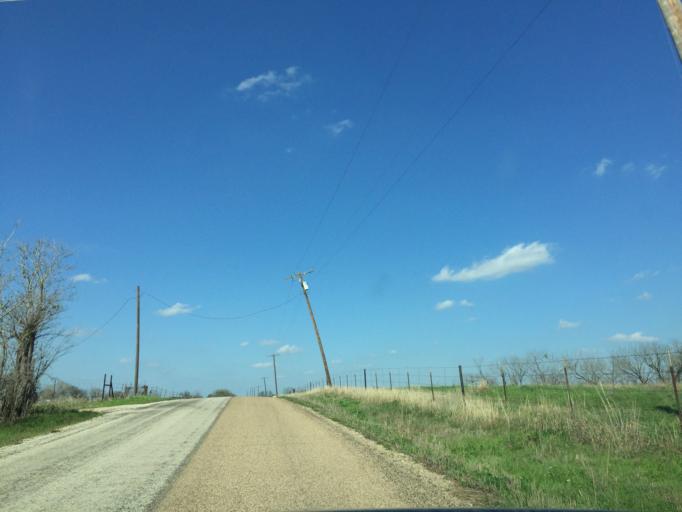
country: US
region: Texas
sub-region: Milam County
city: Thorndale
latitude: 30.5889
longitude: -97.1820
